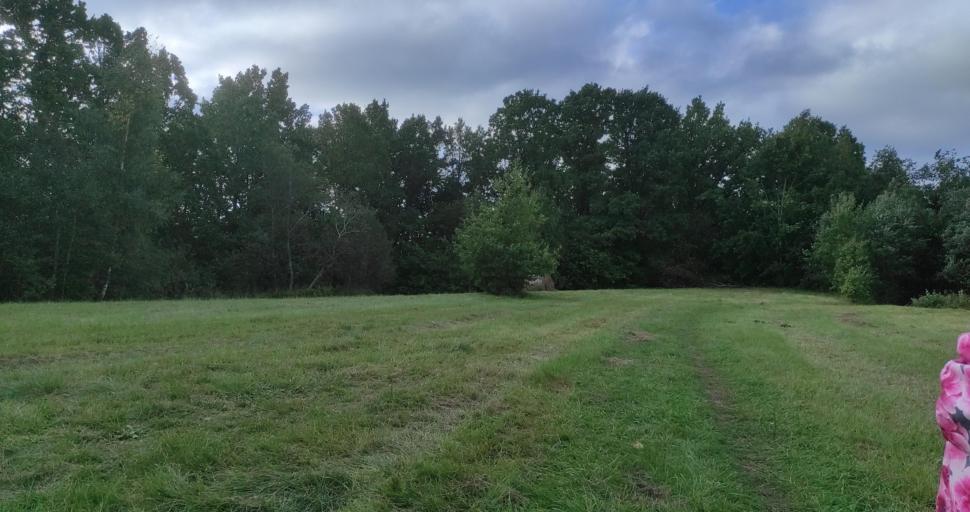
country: LV
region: Kuldigas Rajons
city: Kuldiga
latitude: 56.9928
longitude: 21.9595
